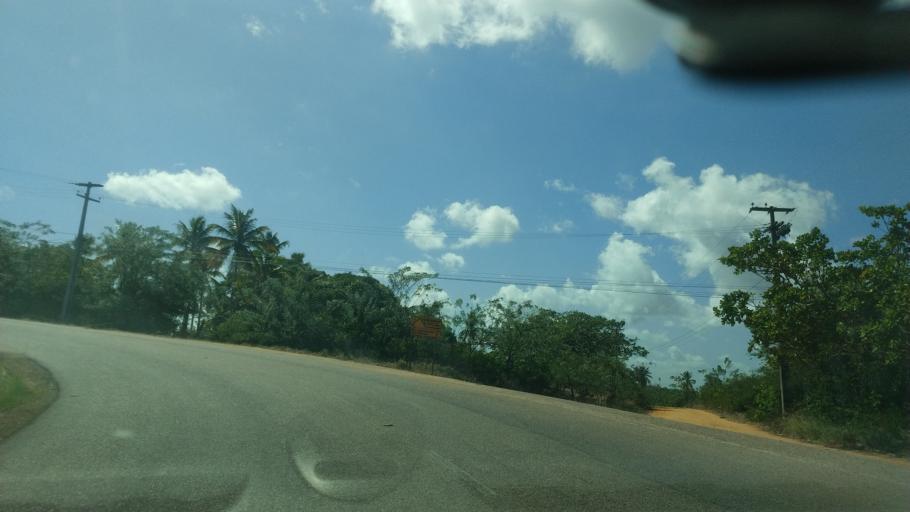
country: BR
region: Rio Grande do Norte
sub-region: Parnamirim
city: Parnamirim
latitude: -5.9408
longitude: -35.1924
